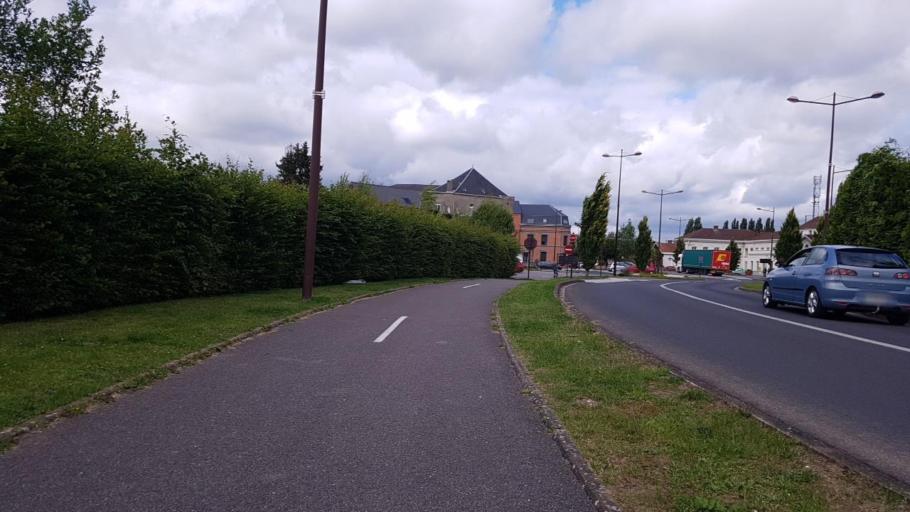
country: FR
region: Picardie
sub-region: Departement de l'Aisne
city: Hirson
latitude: 49.9141
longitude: 4.0825
